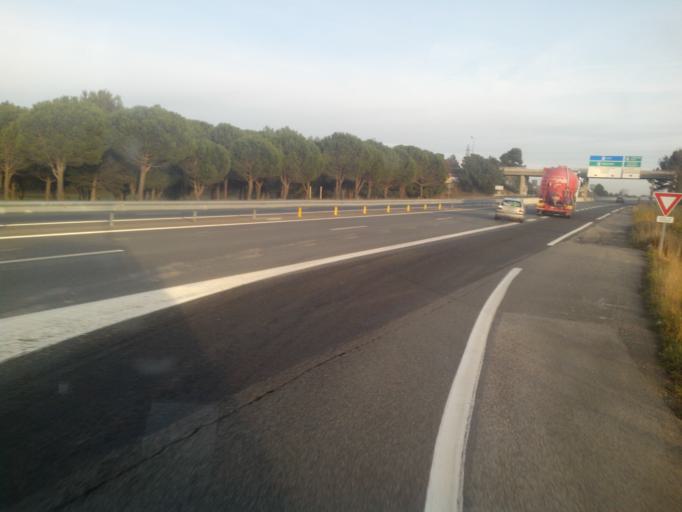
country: FR
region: Languedoc-Roussillon
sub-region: Departement de l'Aude
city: Palaja
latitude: 43.2067
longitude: 2.3873
